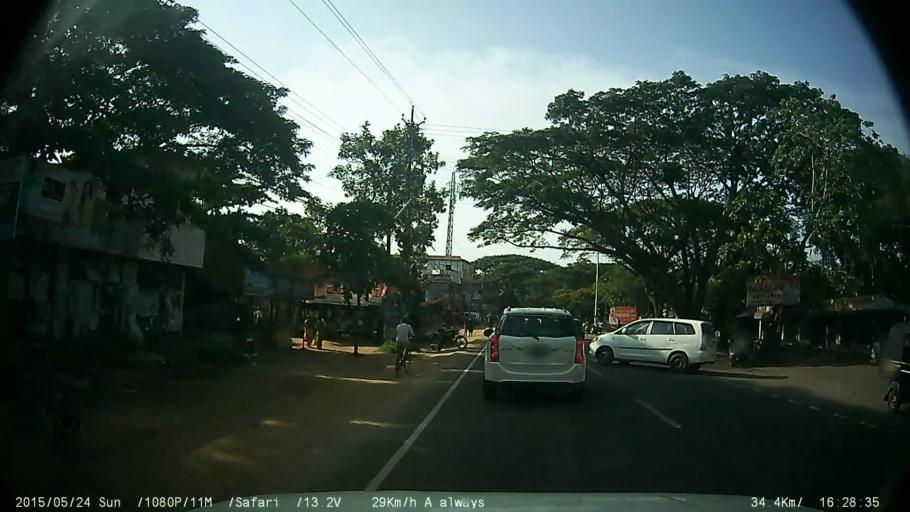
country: IN
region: Kerala
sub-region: Alappuzha
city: Alleppey
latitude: 9.5376
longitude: 76.3272
